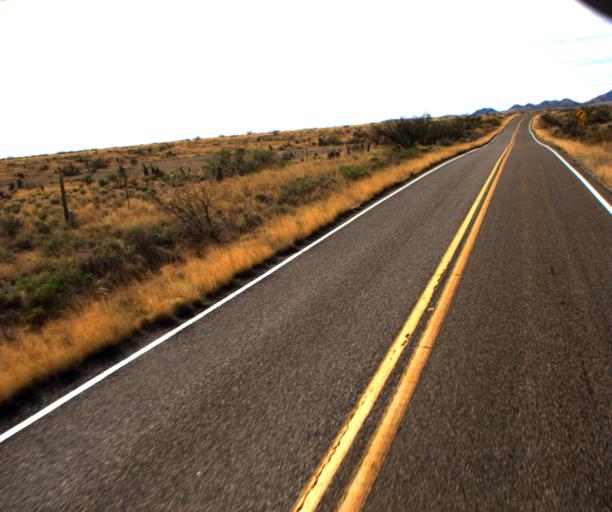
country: US
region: Arizona
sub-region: Cochise County
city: Willcox
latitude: 32.1012
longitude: -109.5425
